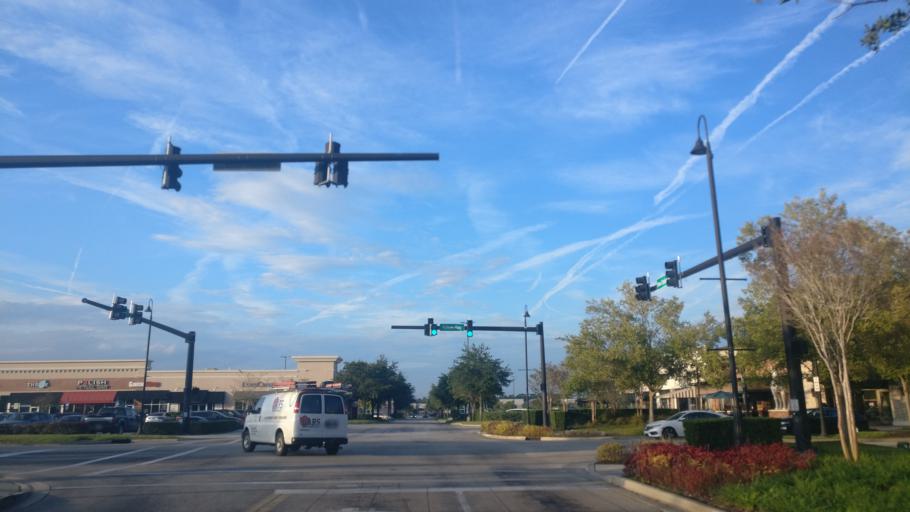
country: US
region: Florida
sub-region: Duval County
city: Jacksonville Beach
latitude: 30.2577
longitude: -81.5272
